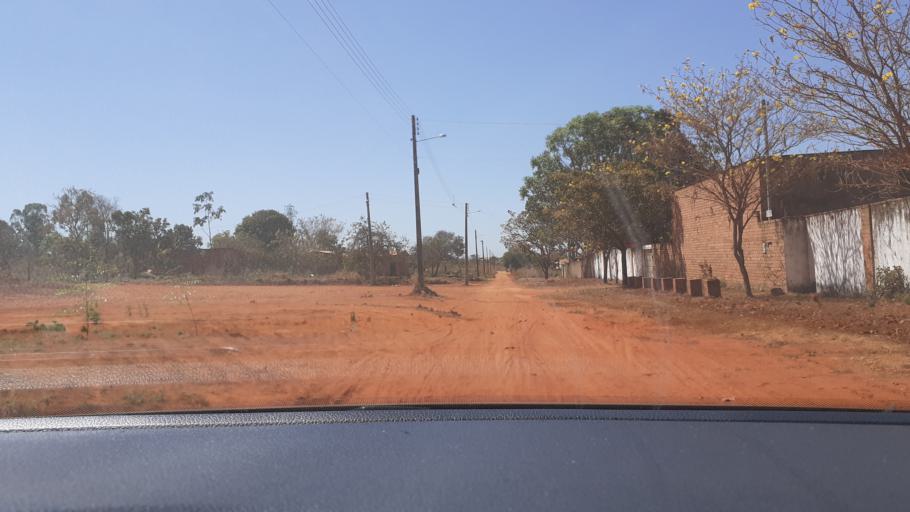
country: BR
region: Goias
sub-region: Aparecida De Goiania
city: Aparecida de Goiania
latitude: -16.8757
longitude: -49.2804
